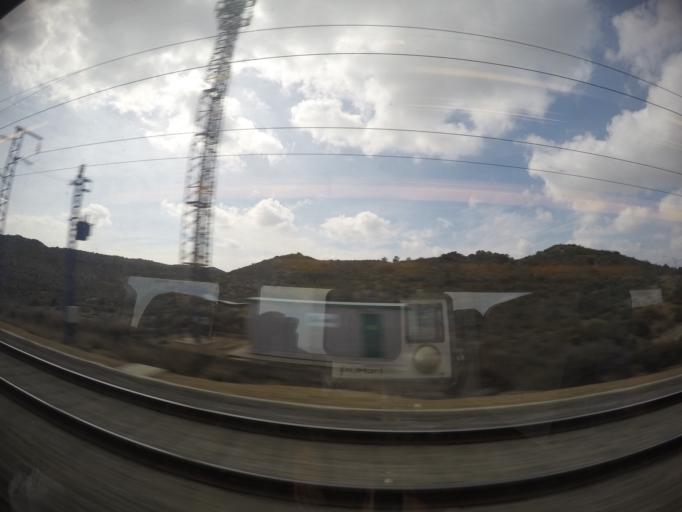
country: ES
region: Aragon
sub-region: Provincia de Huesca
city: Castejon de Monegros
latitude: 41.5311
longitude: -0.3298
